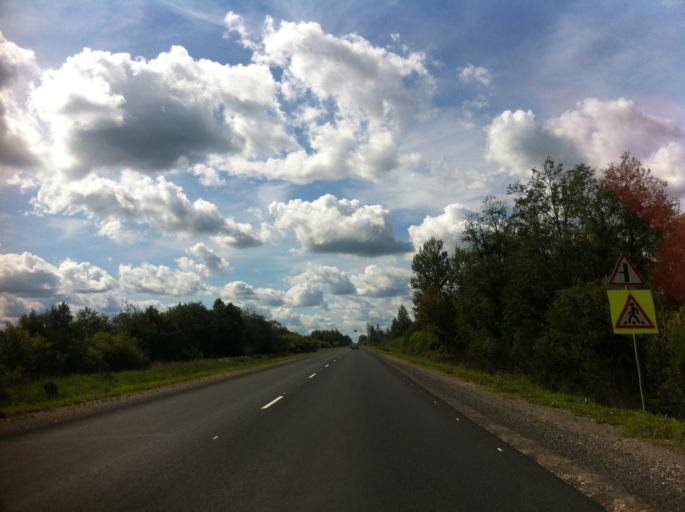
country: RU
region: Pskov
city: Izborsk
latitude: 57.7411
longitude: 28.0133
